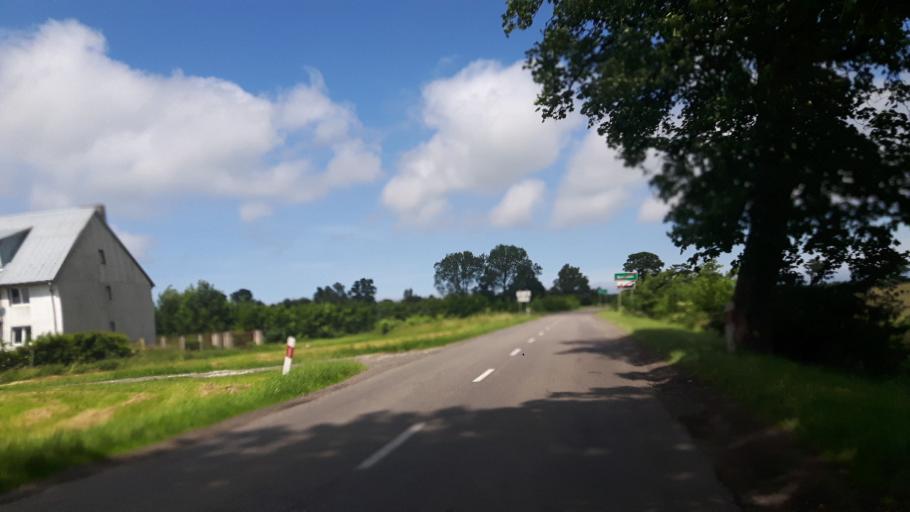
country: PL
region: Pomeranian Voivodeship
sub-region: Powiat slupski
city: Ustka
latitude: 54.5436
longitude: 16.8238
